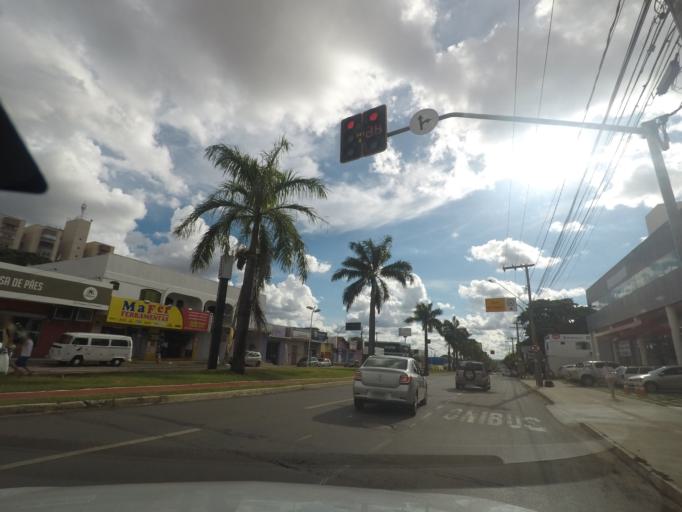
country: BR
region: Goias
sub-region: Goiania
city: Goiania
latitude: -16.7157
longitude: -49.2829
